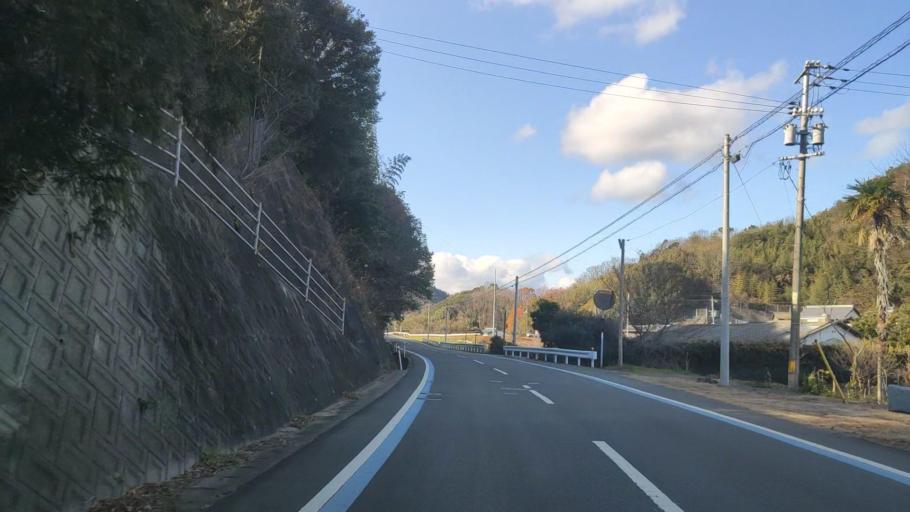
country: JP
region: Hiroshima
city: Innoshima
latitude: 34.2300
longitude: 133.1061
